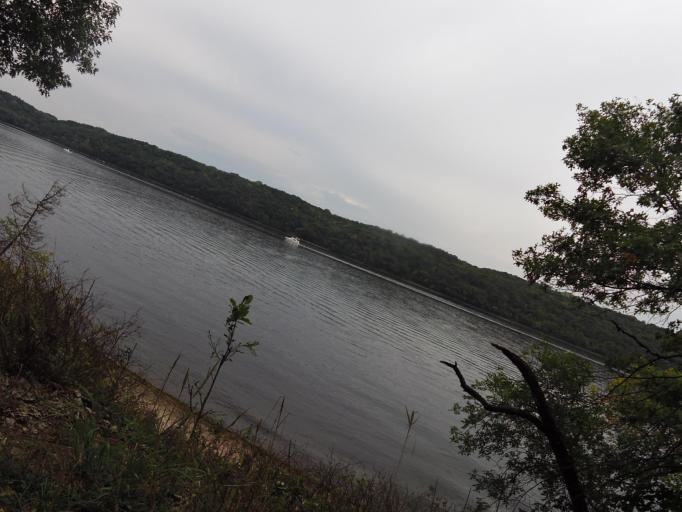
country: US
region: Minnesota
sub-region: Washington County
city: Afton
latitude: 44.8677
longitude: -92.7713
